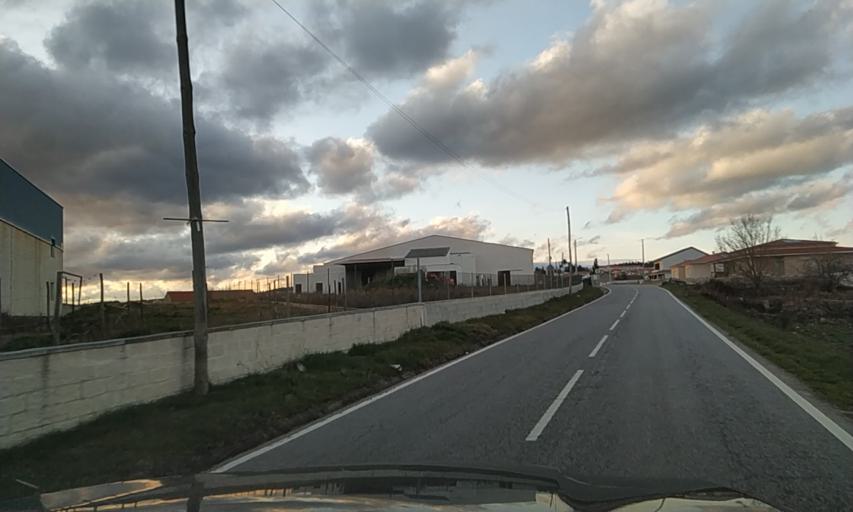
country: PT
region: Braganca
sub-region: Carrazeda de Ansiaes
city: Carrazeda de Anciaes
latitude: 41.2335
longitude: -7.3041
